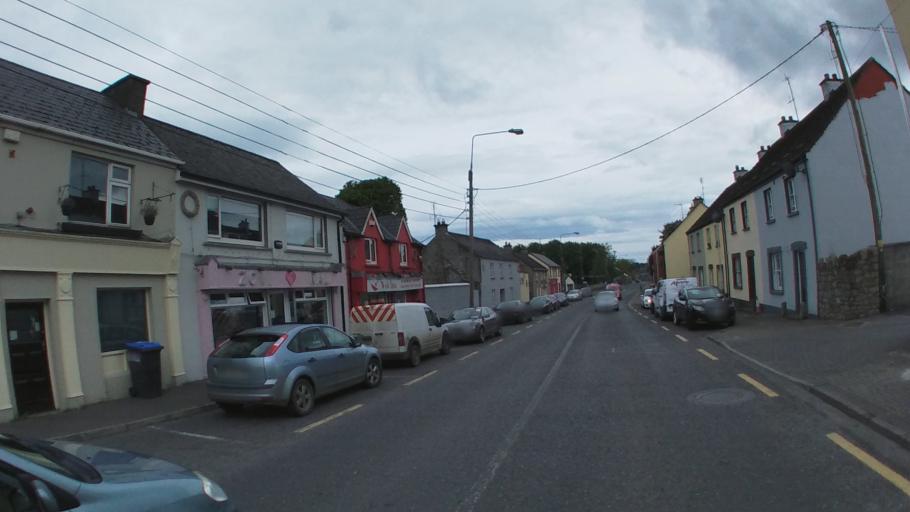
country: IE
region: Leinster
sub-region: Kildare
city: Castledermot
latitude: 52.9110
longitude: -6.8378
